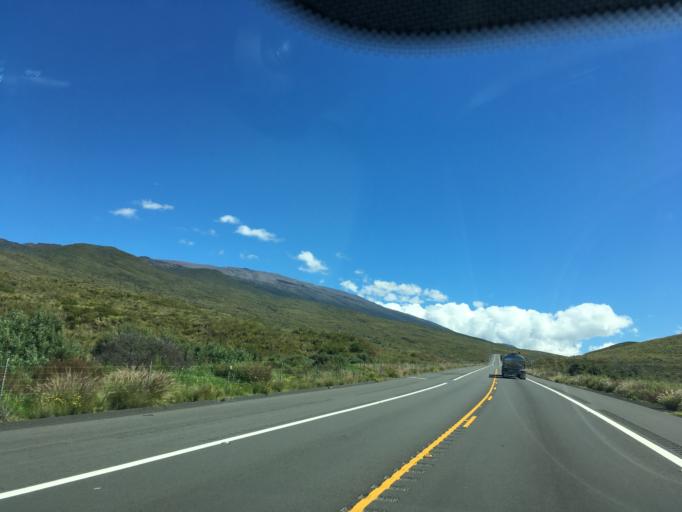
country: US
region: Hawaii
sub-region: Hawaii County
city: Waikoloa
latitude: 19.7810
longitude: -155.6128
